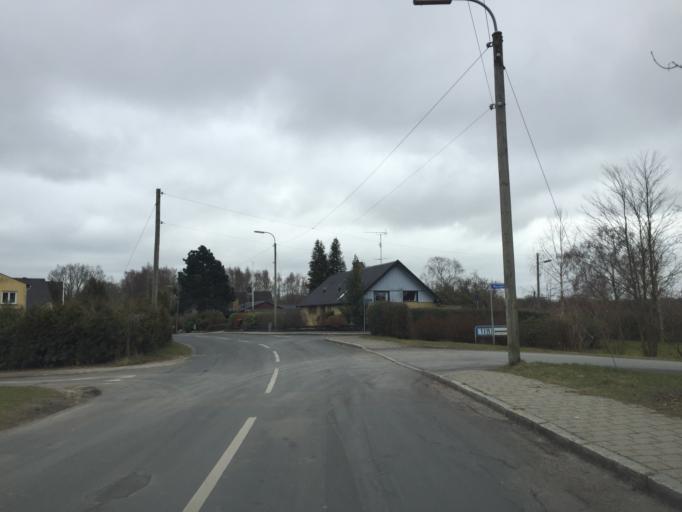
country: DK
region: Capital Region
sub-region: Allerod Kommune
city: Lillerod
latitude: 55.9042
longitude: 12.3299
